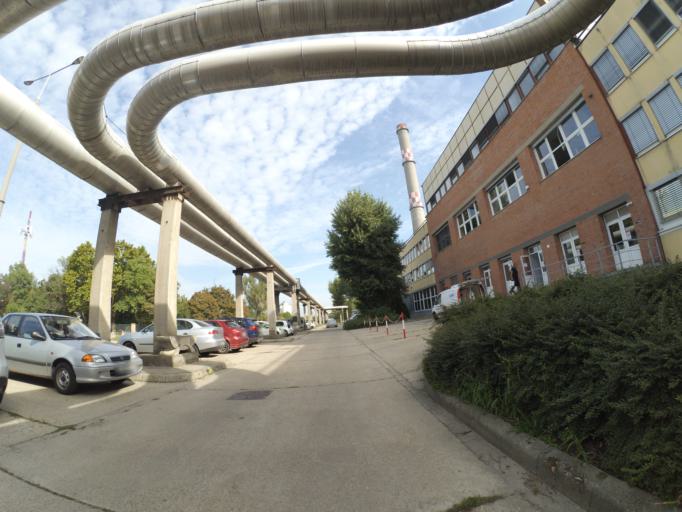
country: HU
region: Budapest
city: Budapest III. keruelet
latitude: 47.5619
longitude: 19.0358
